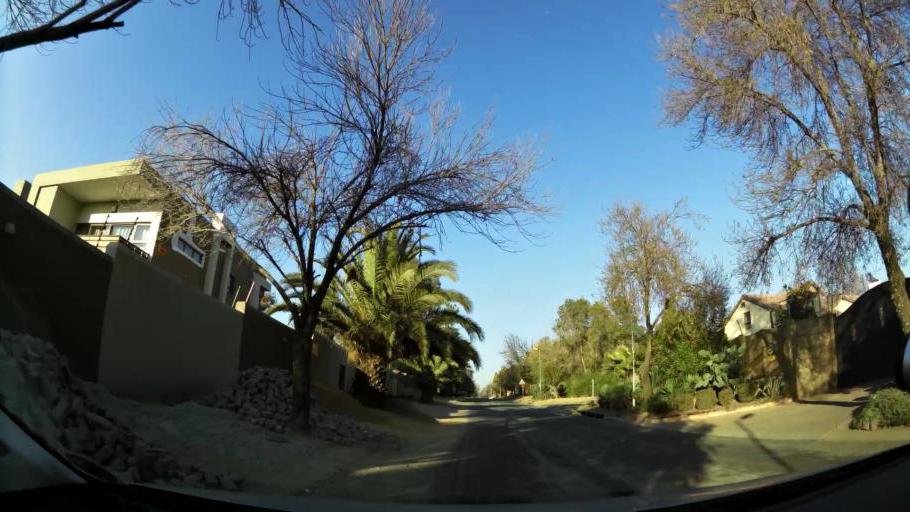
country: ZA
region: Gauteng
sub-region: City of Johannesburg Metropolitan Municipality
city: Midrand
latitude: -26.0439
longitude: 28.1064
